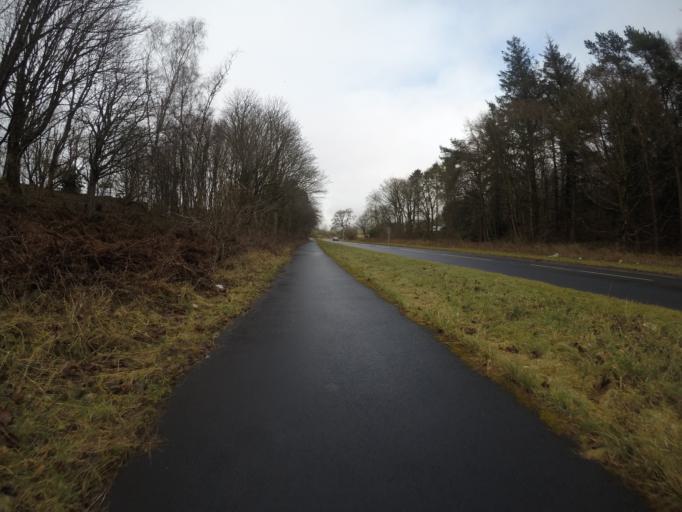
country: GB
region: Scotland
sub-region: North Ayrshire
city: Fairlie
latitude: 55.7302
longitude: -4.8648
